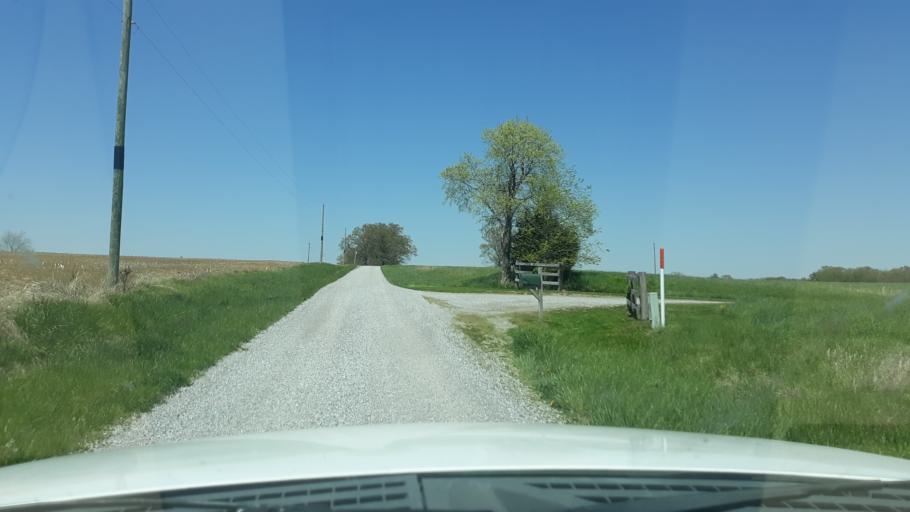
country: US
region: Illinois
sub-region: Saline County
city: Harrisburg
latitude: 37.8827
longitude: -88.6421
